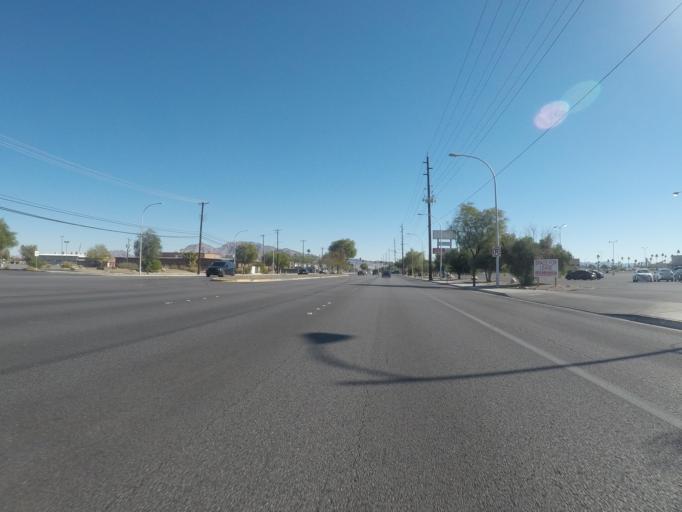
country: US
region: Nevada
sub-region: Clark County
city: Winchester
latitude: 36.1442
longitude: -115.1122
